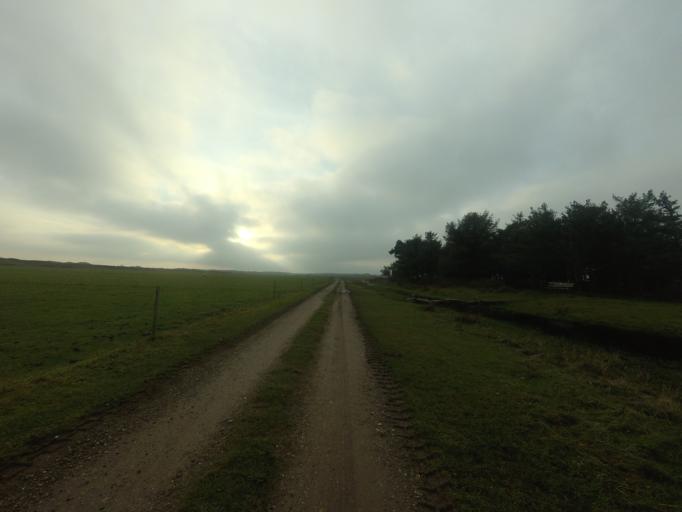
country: NL
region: North Holland
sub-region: Gemeente Texel
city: Den Burg
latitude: 53.1153
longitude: 4.7895
